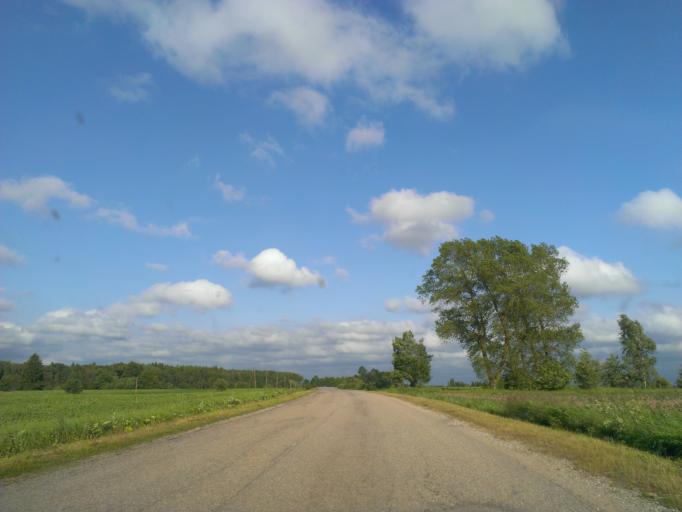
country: LV
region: Aizpute
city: Aizpute
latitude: 56.7560
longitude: 21.5523
